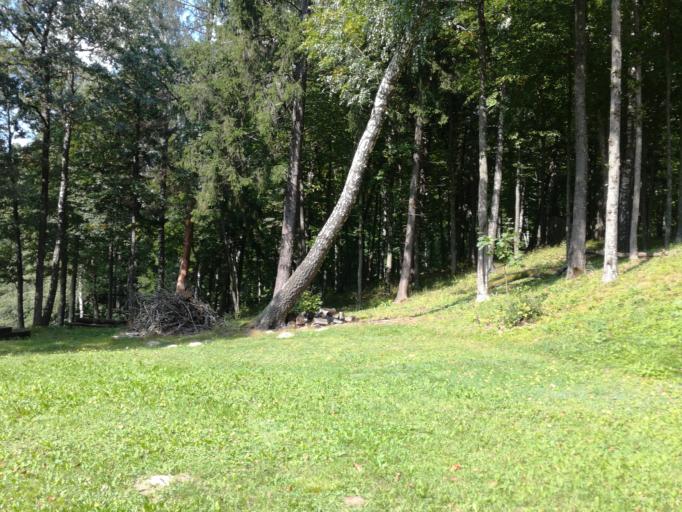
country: LT
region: Alytaus apskritis
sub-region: Alytus
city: Alytus
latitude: 54.2681
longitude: 24.0874
